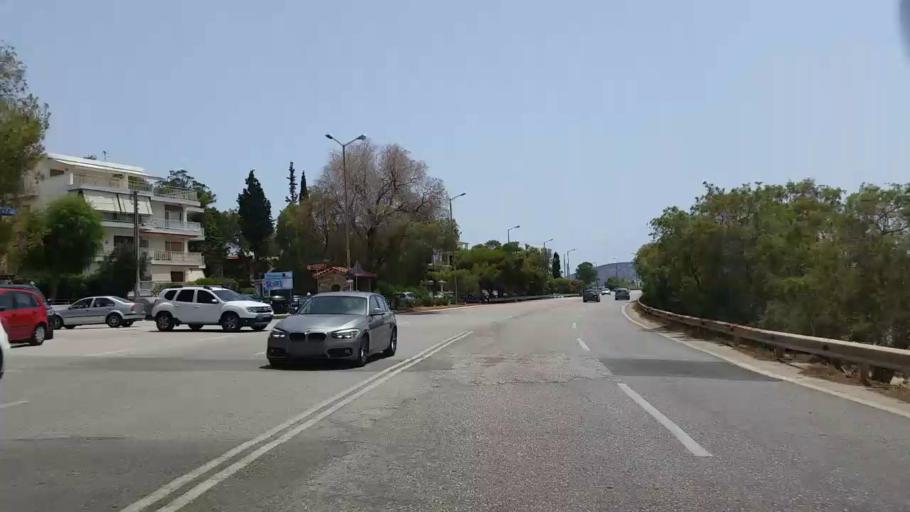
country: GR
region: Attica
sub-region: Nomarchia Anatolikis Attikis
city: Saronida
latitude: 37.7421
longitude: 23.9048
